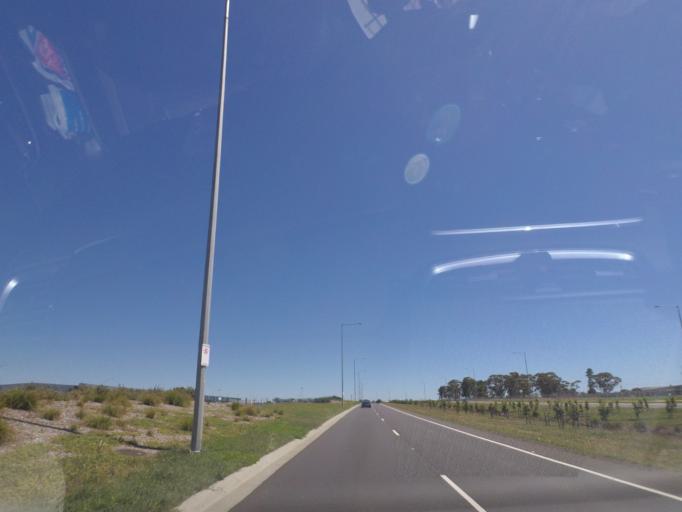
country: AU
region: Victoria
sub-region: Hume
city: Tullamarine
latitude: -37.6887
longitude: 144.8653
